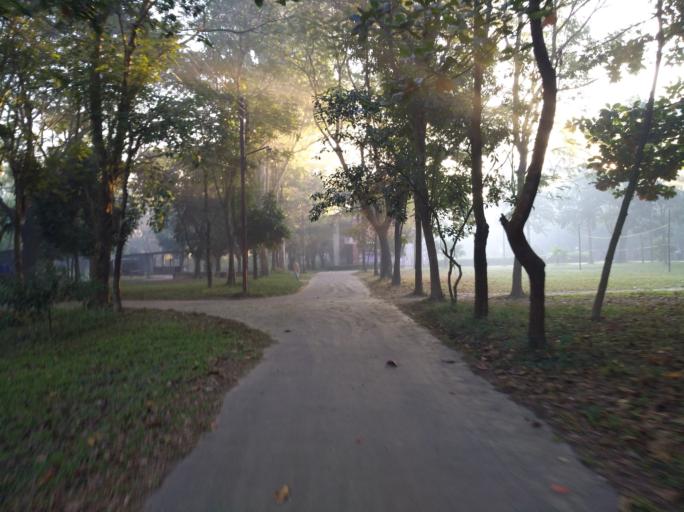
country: BD
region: Dhaka
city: Tungi
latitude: 23.8761
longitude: 90.2708
